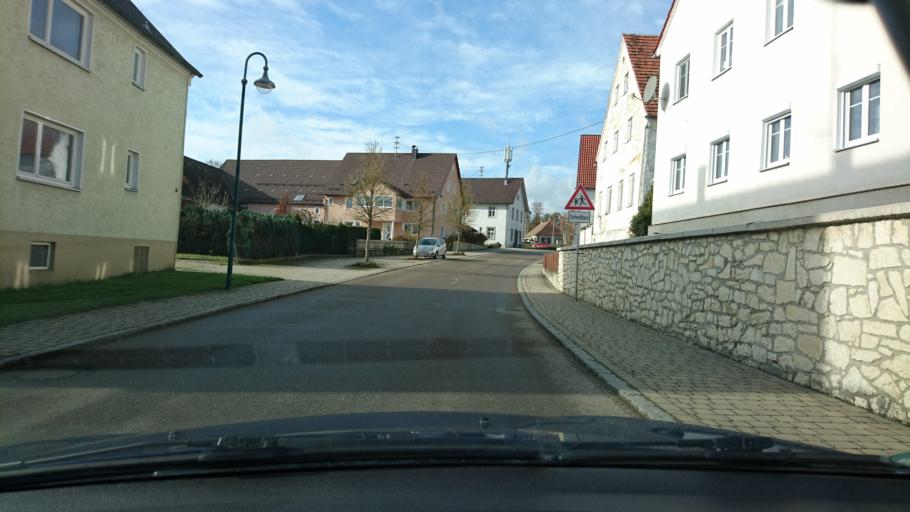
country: DE
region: Bavaria
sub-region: Swabia
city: Amerdingen
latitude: 48.7256
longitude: 10.4861
